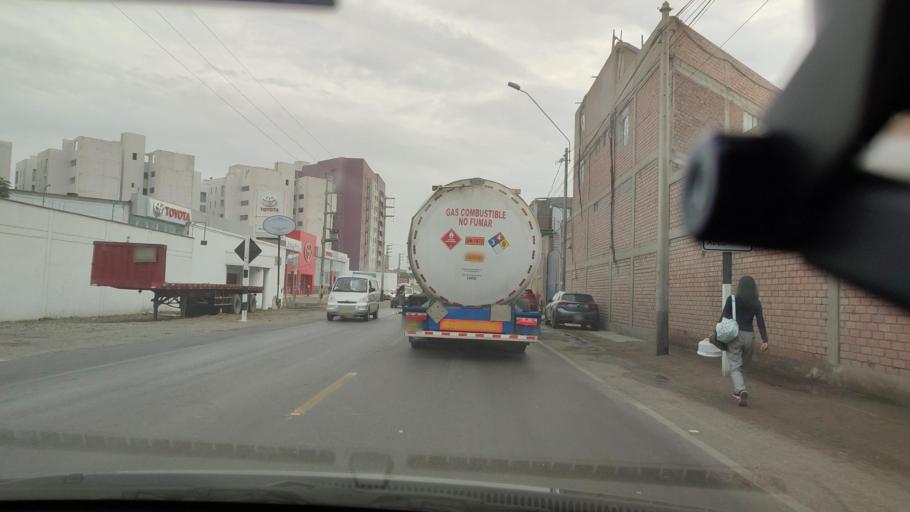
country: PE
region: La Libertad
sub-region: Provincia de Trujillo
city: Buenos Aires
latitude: -8.1407
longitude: -79.0275
